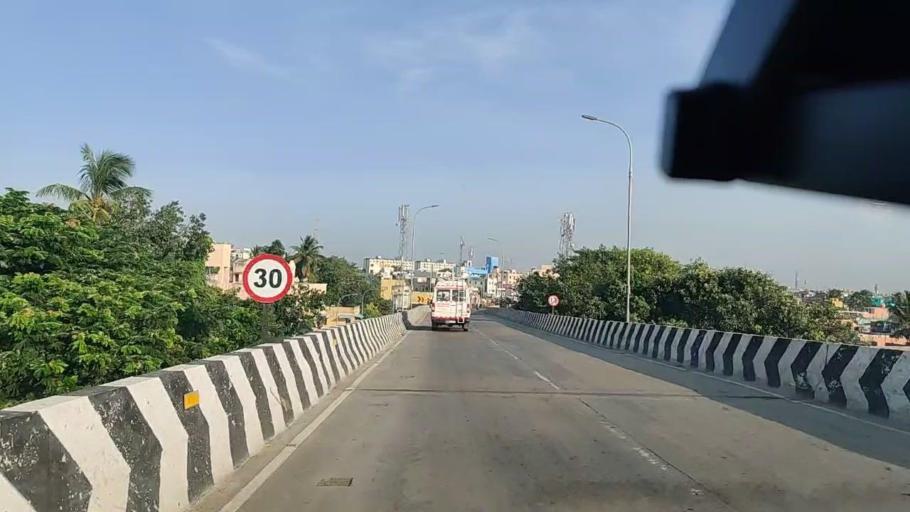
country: IN
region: Tamil Nadu
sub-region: Chennai
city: George Town
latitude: 13.1112
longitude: 80.2653
